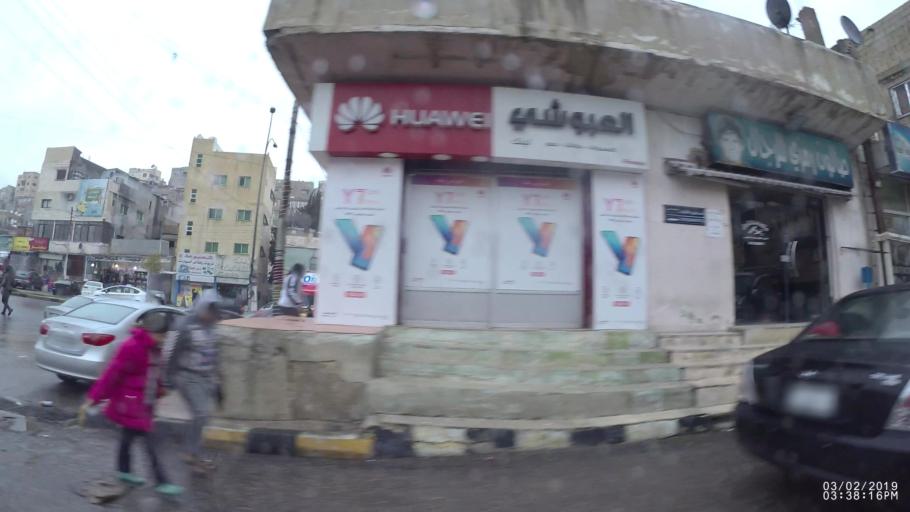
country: JO
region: Amman
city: Amman
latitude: 31.9732
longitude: 35.9229
